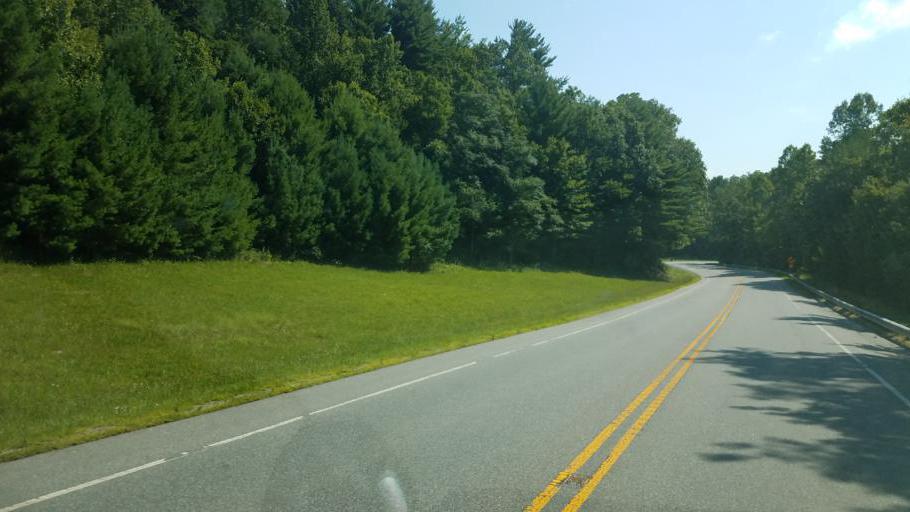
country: US
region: North Carolina
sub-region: Avery County
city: Newland
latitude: 35.9551
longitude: -81.8548
